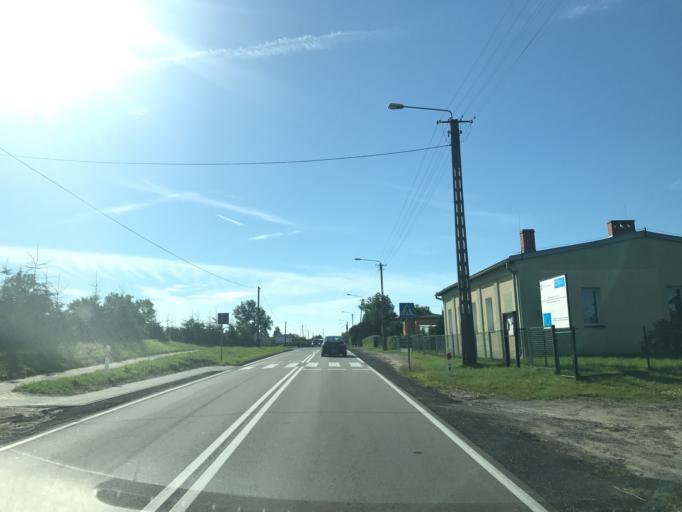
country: PL
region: Pomeranian Voivodeship
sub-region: Powiat czluchowski
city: Czluchow
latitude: 53.6858
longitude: 17.3290
